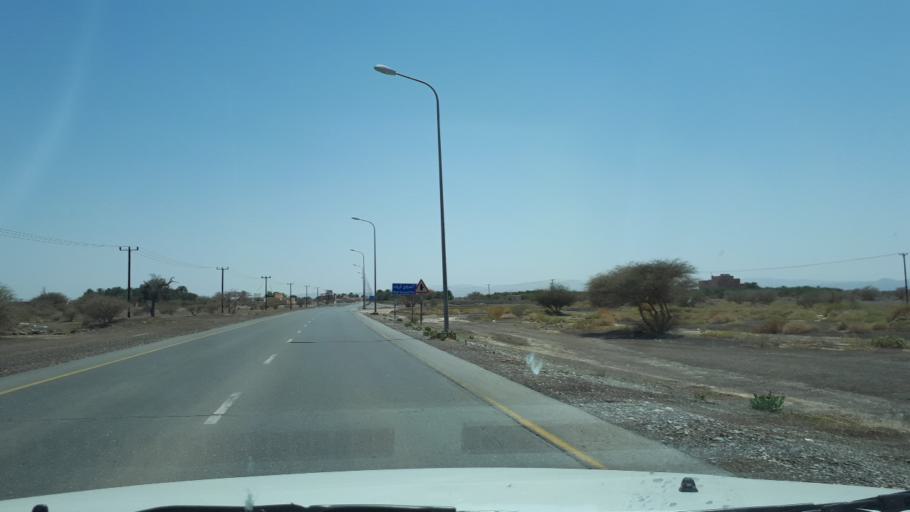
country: OM
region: Muhafazat ad Dakhiliyah
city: Bahla'
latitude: 22.9202
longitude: 57.2547
